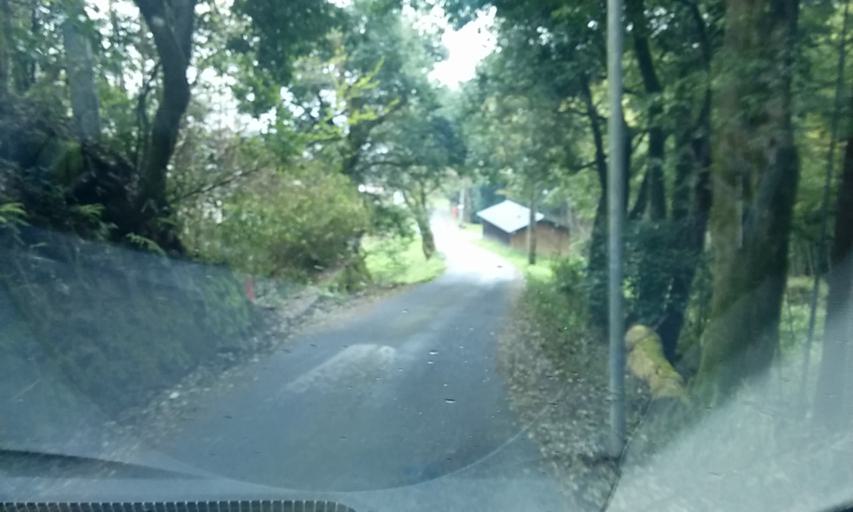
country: JP
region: Kyoto
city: Miyazu
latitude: 35.5854
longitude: 135.1986
